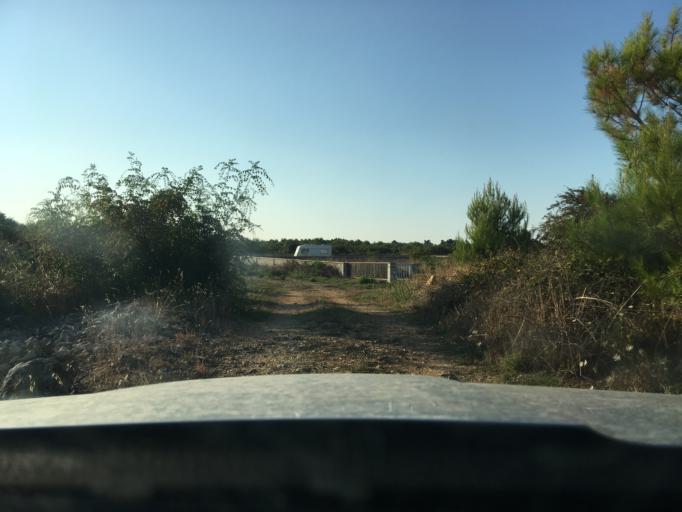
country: HR
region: Zadarska
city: Vir
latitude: 44.2980
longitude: 15.0749
